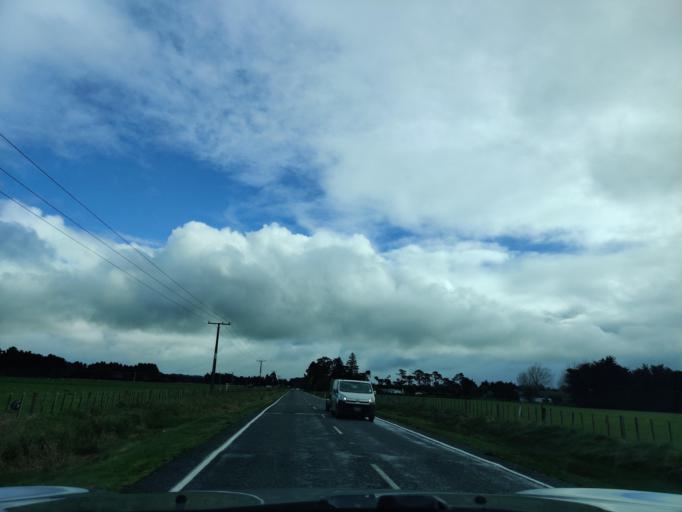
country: NZ
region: Hawke's Bay
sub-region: Hastings District
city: Hastings
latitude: -40.0196
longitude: 176.3420
